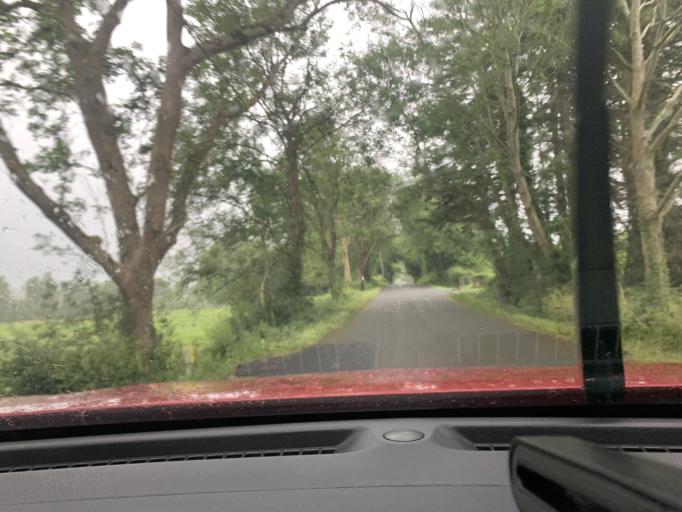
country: GB
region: Northern Ireland
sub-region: Fermanagh District
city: Enniskillen
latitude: 54.2889
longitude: -7.7121
